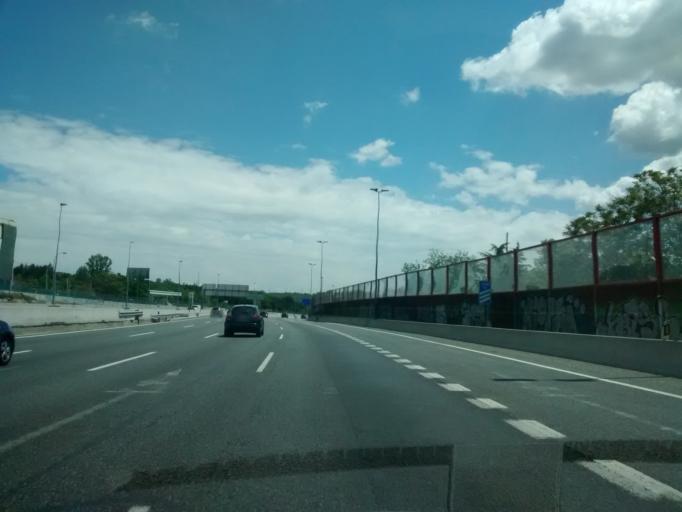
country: ES
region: Madrid
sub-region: Provincia de Madrid
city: Collado-Villalba
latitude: 40.6295
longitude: -3.9981
